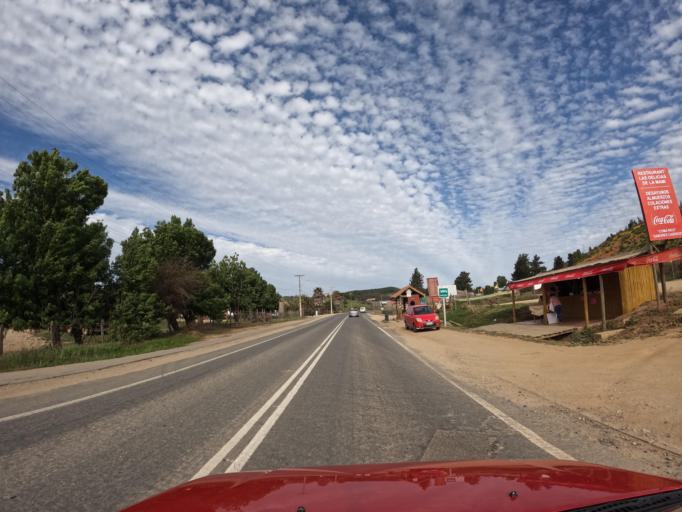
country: CL
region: O'Higgins
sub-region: Provincia de Colchagua
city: Santa Cruz
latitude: -34.3034
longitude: -71.7870
